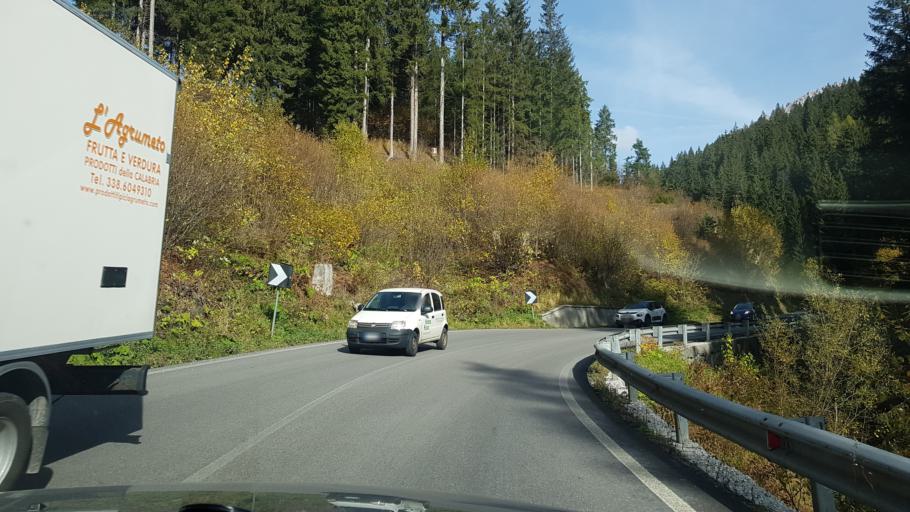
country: IT
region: Veneto
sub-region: Provincia di Belluno
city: Candide
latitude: 46.5976
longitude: 12.5233
